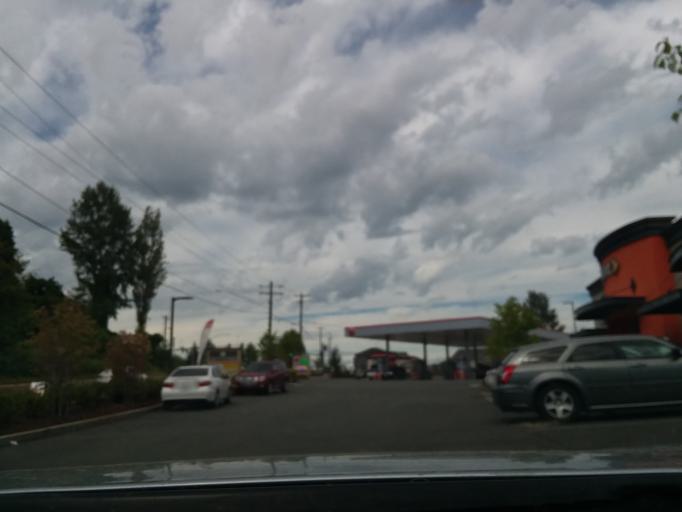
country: US
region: Washington
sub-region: Snohomish County
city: West Lake Stevens
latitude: 47.9783
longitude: -122.1230
